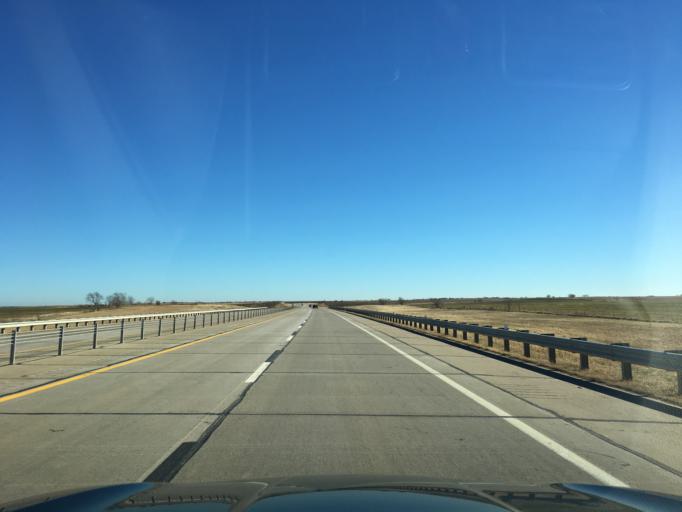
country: US
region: Oklahoma
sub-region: Noble County
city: Perry
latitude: 36.3987
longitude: -97.2378
